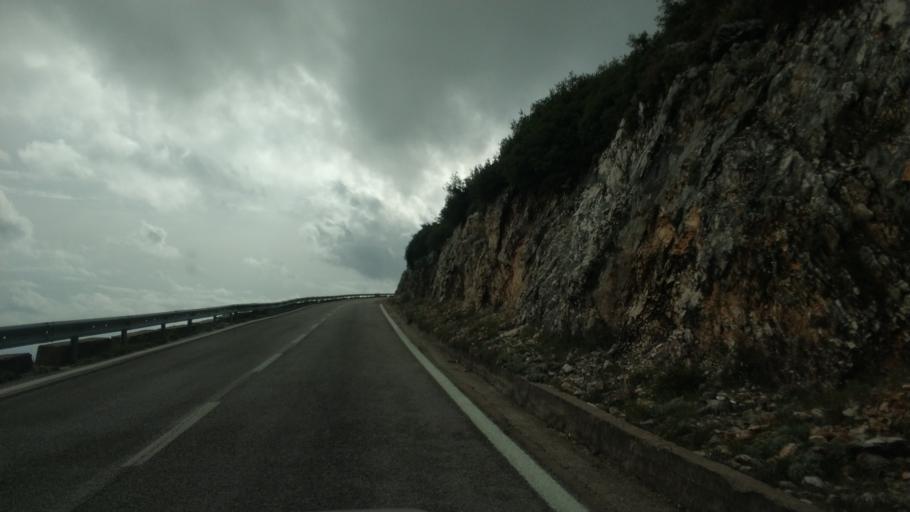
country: AL
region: Vlore
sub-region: Rrethi i Vlores
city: Vranisht
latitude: 40.1840
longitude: 19.6043
